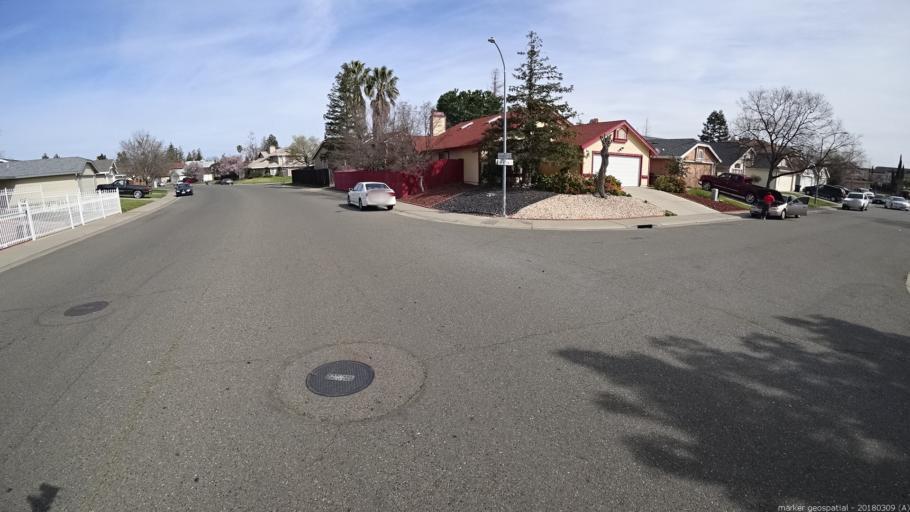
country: US
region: California
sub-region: Sacramento County
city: Florin
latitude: 38.4555
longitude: -121.3953
